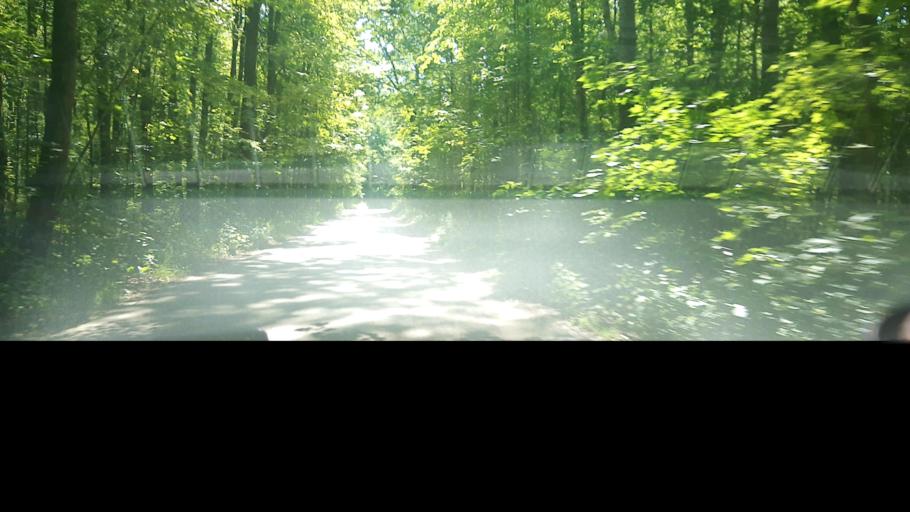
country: RU
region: Nizjnij Novgorod
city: Afonino
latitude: 56.2674
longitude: 44.2010
